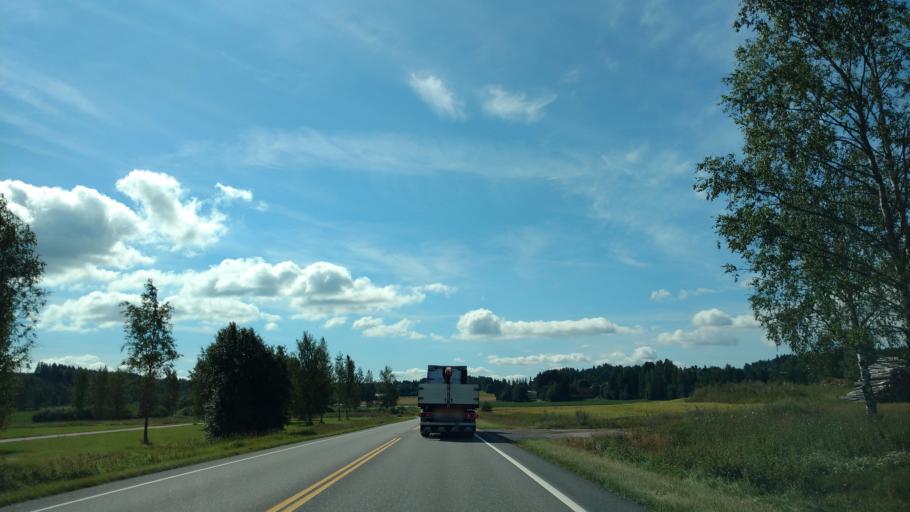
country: FI
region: Varsinais-Suomi
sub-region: Salo
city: Pernioe
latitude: 60.2668
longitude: 23.1286
